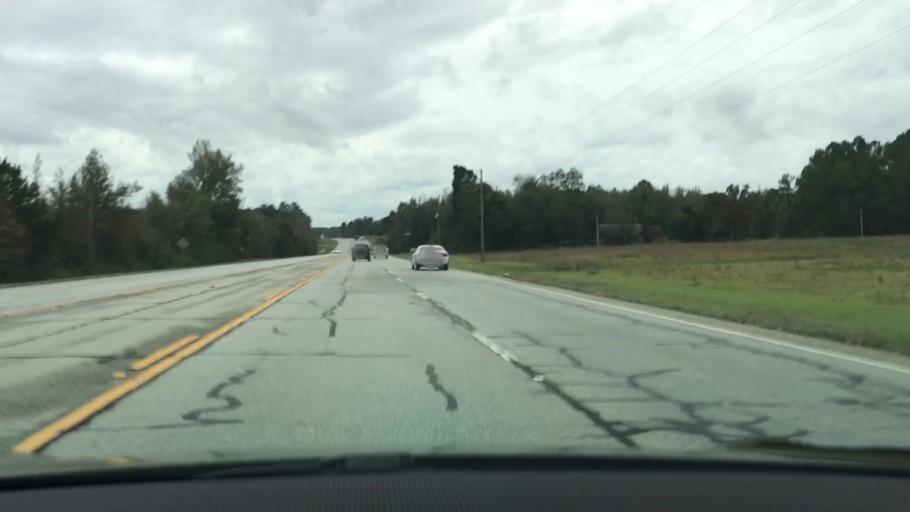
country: US
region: Georgia
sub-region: Jefferson County
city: Wadley
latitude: 32.8805
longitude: -82.3960
